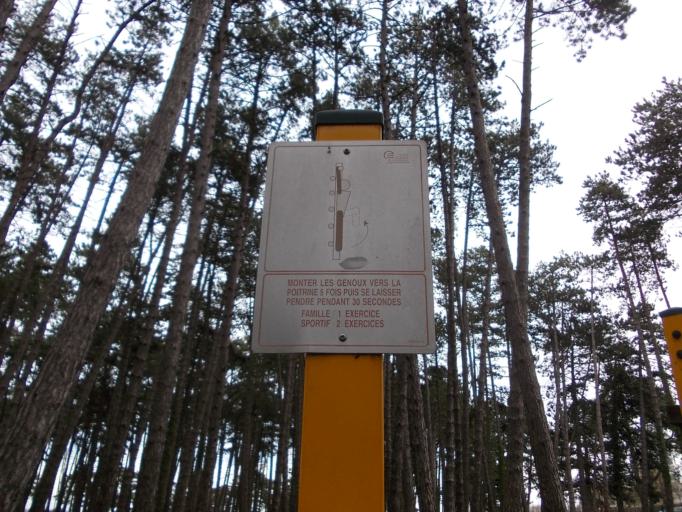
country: FR
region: Lorraine
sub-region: Departement de Meurthe-et-Moselle
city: Villers-les-Nancy
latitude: 48.6553
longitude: 6.1591
